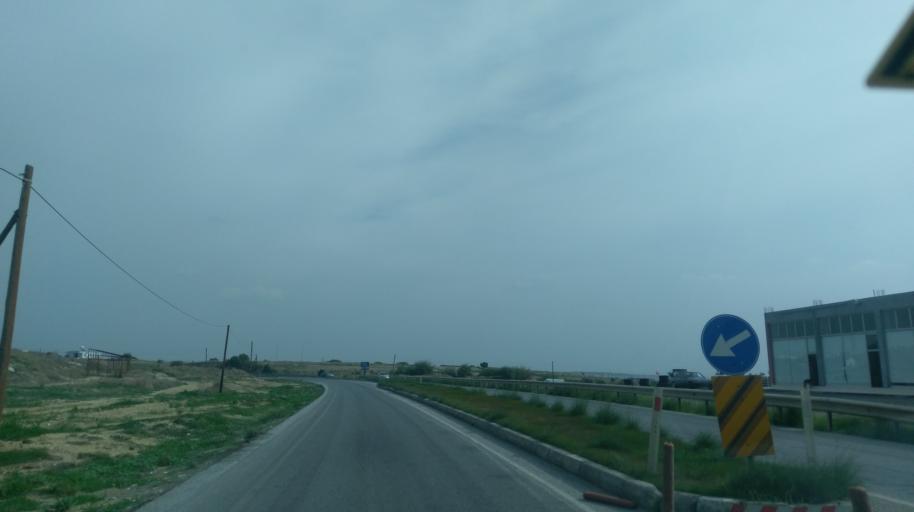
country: CY
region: Larnaka
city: Athienou
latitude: 35.2296
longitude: 33.5527
